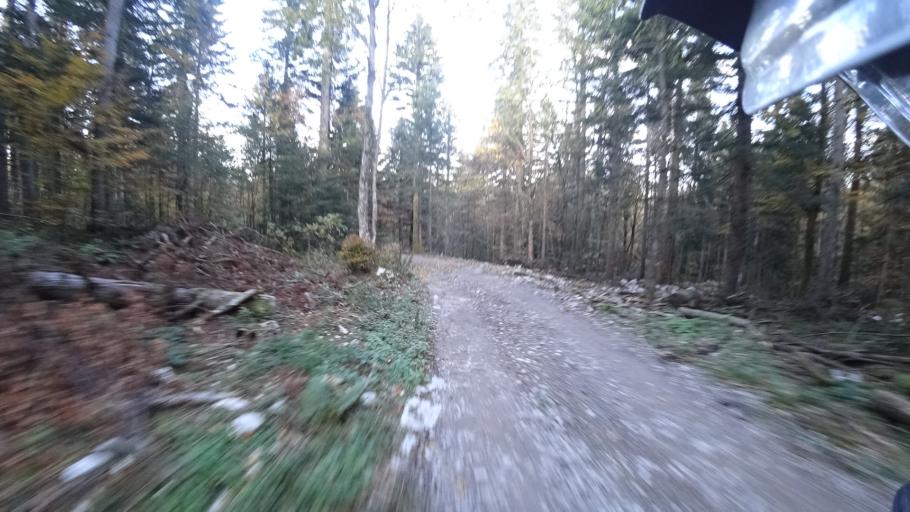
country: HR
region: Karlovacka
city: Plaski
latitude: 44.9571
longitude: 15.4341
